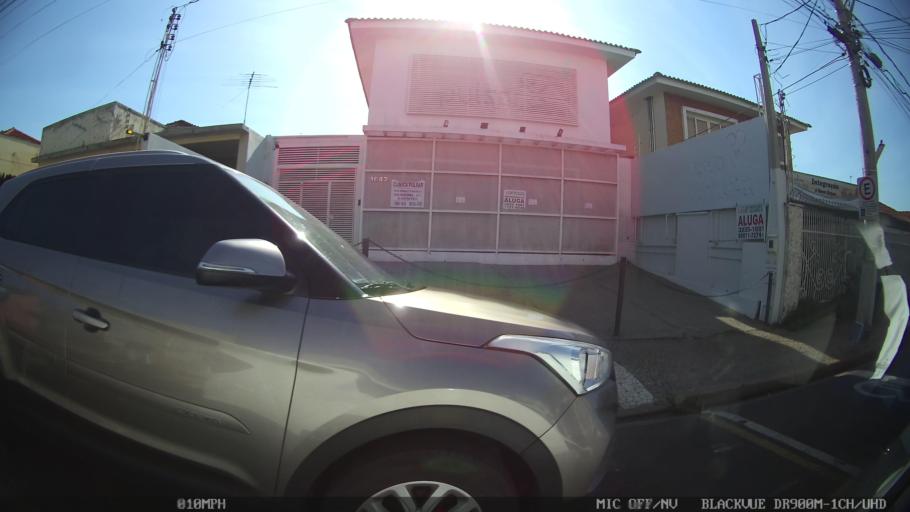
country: BR
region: Sao Paulo
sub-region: Sao Jose Do Rio Preto
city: Sao Jose do Rio Preto
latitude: -20.8025
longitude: -49.3849
